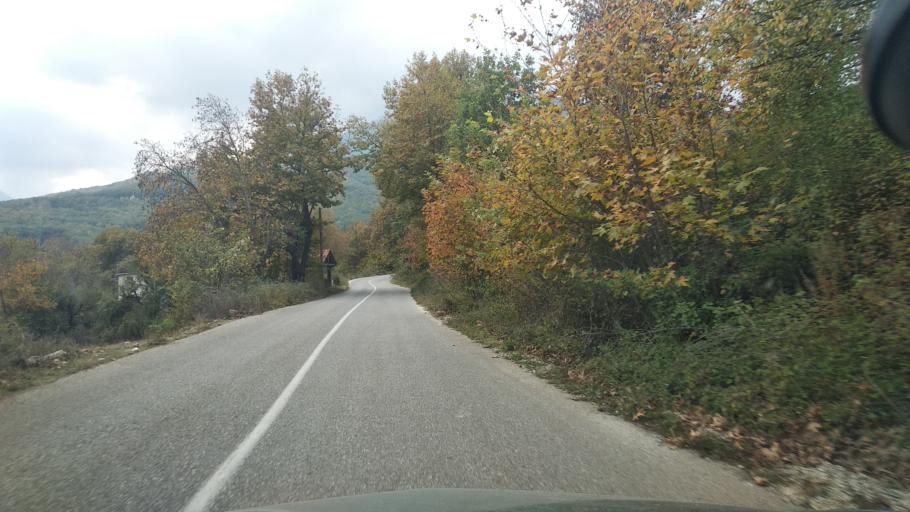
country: GR
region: Thessaly
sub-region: Trikala
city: Kastraki
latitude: 39.6707
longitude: 21.5079
